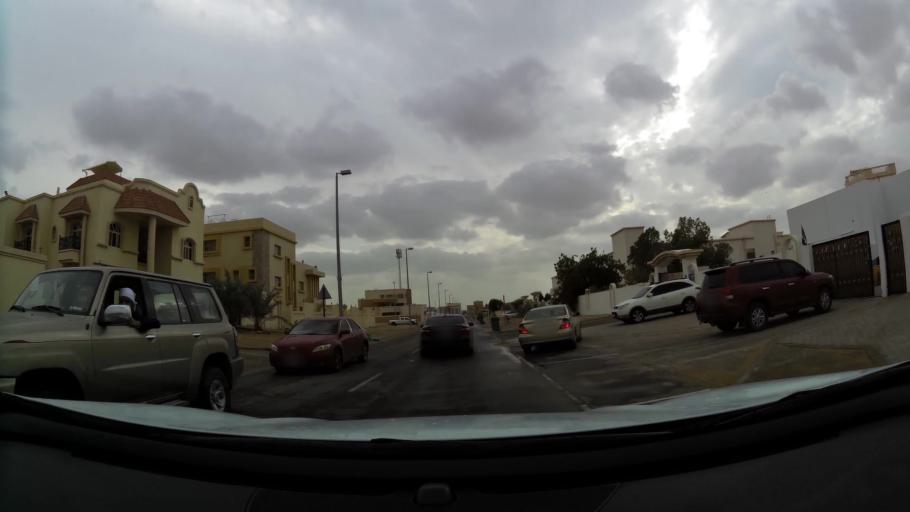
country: AE
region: Abu Dhabi
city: Abu Dhabi
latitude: 24.3544
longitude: 54.6281
